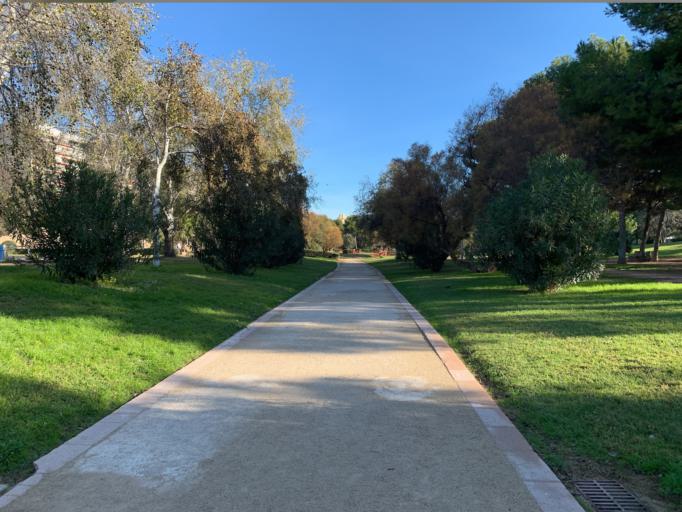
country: ES
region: Valencia
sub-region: Provincia de Valencia
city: Valencia
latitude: 39.4797
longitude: -0.3864
